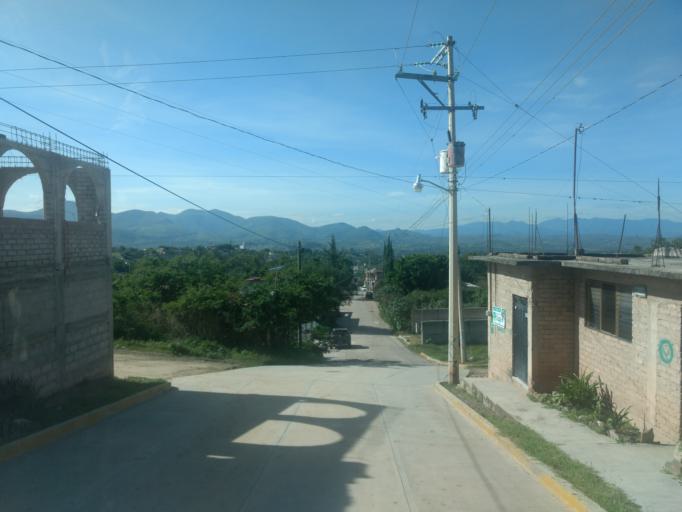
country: MX
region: Oaxaca
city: Ciudad de Huajuapam de Leon
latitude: 17.8262
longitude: -97.7879
